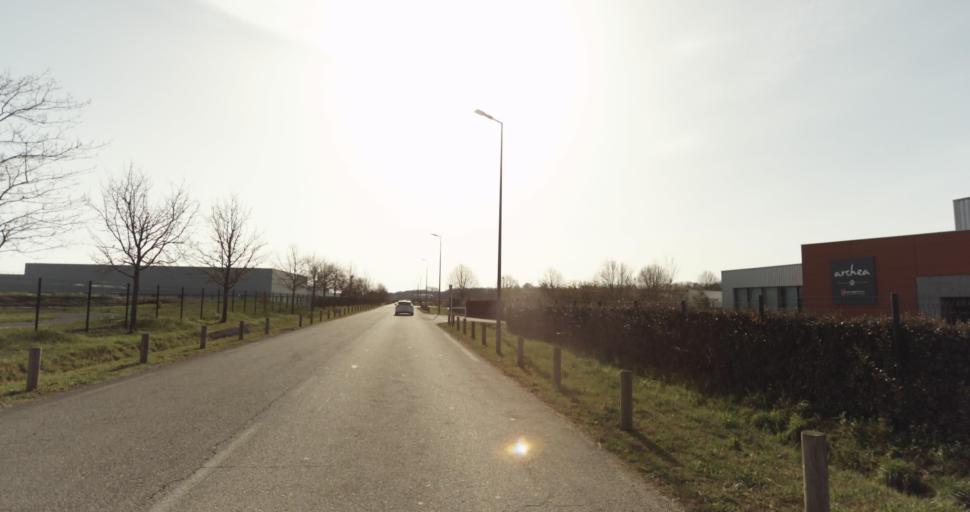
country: FR
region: Midi-Pyrenees
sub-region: Departement du Tarn
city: Saint-Sulpice-la-Pointe
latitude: 43.7641
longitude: 1.7116
